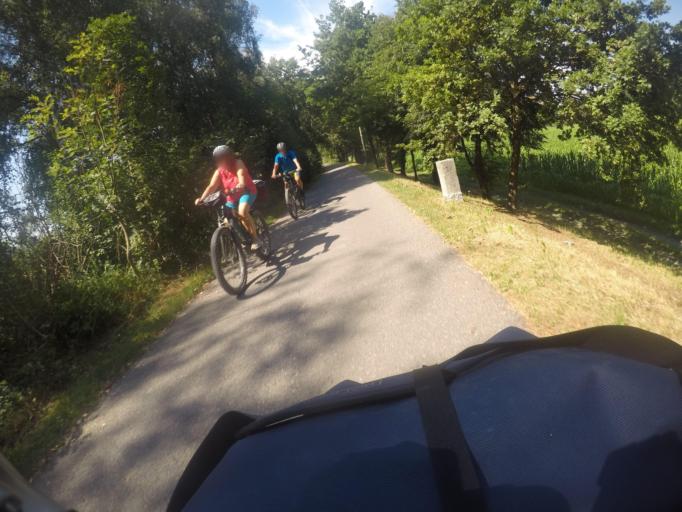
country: CH
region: Saint Gallen
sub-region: Wahlkreis Rheintal
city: Diepoldsau
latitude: 47.3902
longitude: 9.6761
